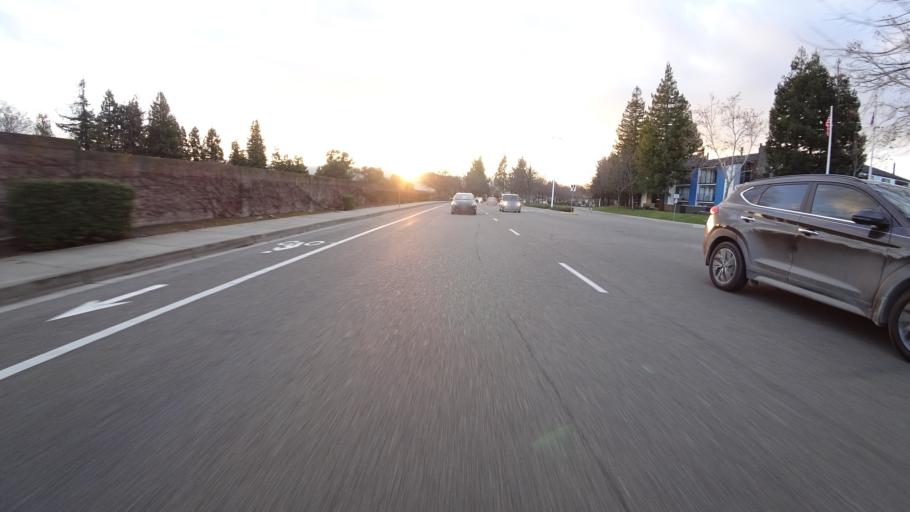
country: US
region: California
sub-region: Alameda County
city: Pleasanton
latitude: 37.6882
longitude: -121.8820
